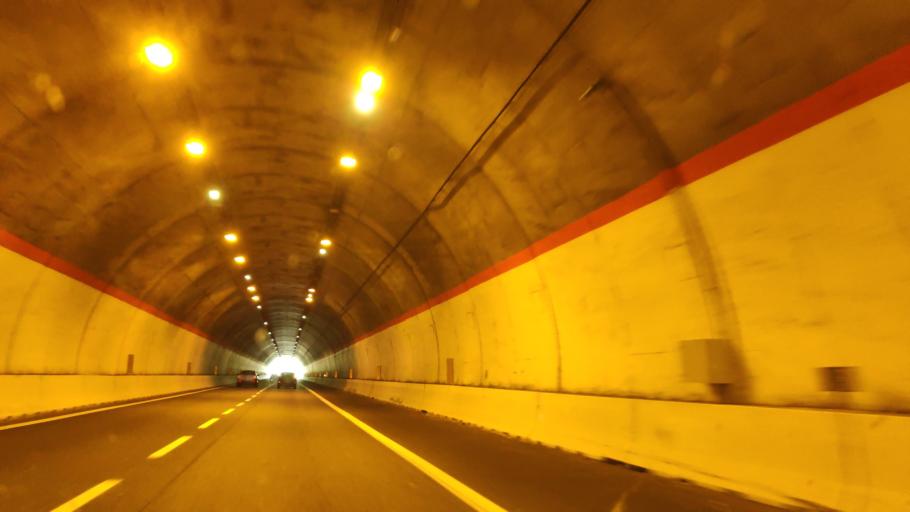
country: IT
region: Campania
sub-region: Provincia di Salerno
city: Auletta
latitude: 40.5348
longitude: 15.4228
